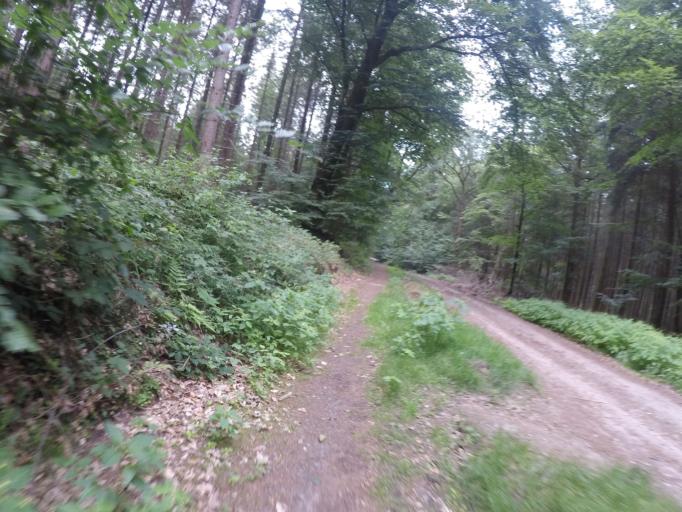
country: DE
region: Lower Saxony
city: Wingst
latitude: 53.7236
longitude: 9.0681
